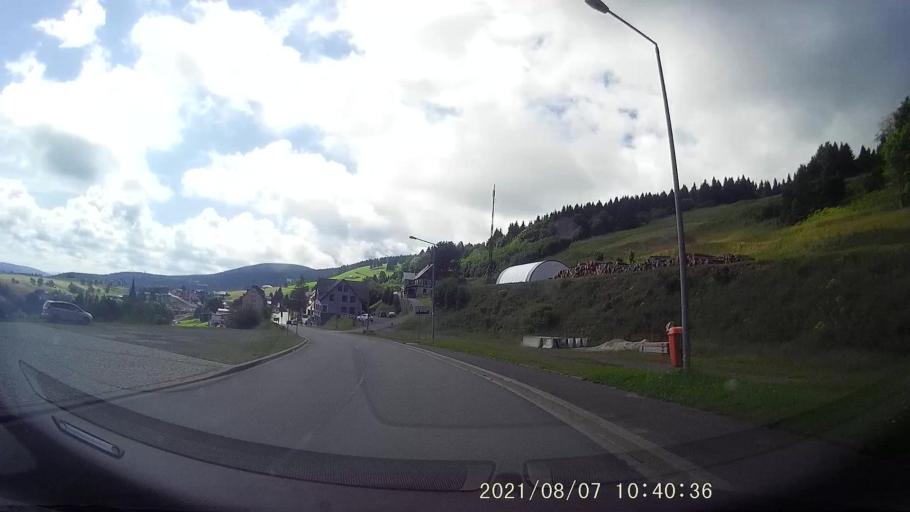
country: PL
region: Lower Silesian Voivodeship
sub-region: Powiat klodzki
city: Duszniki-Zdroj
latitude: 50.3429
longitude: 16.3816
